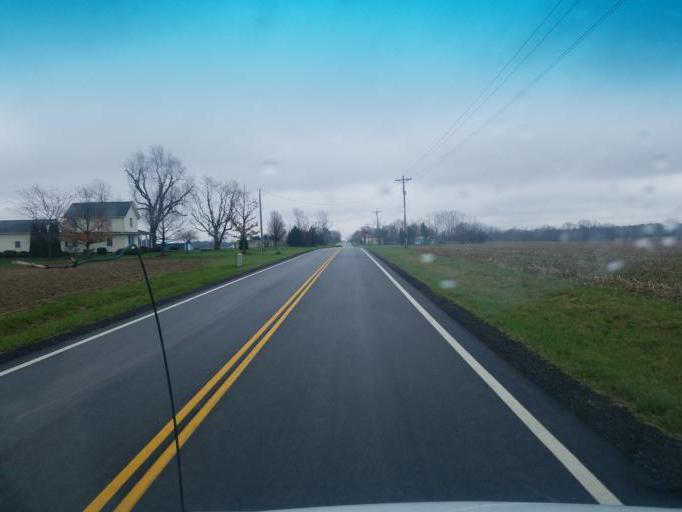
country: US
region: Ohio
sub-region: Huron County
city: Willard
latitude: 40.9600
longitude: -82.8000
